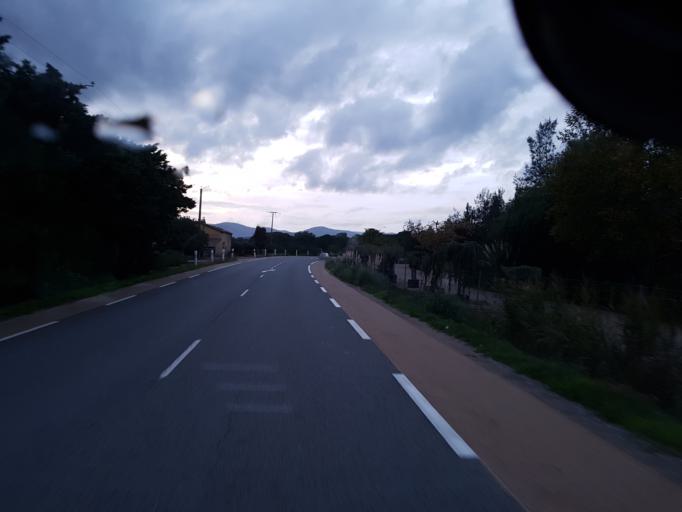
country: FR
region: Provence-Alpes-Cote d'Azur
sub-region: Departement du Var
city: Grimaud
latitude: 43.2698
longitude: 6.5444
